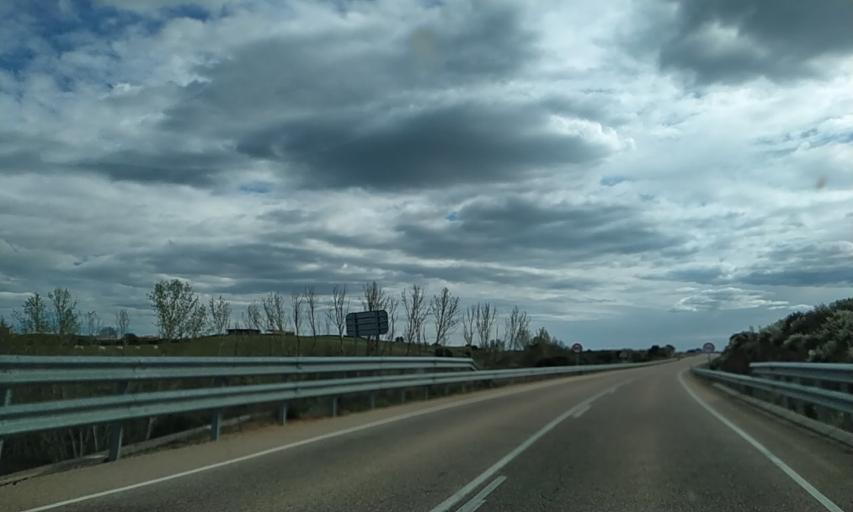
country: ES
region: Castille and Leon
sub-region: Provincia de Salamanca
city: Herguijuela de Ciudad Rodrigo
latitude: 40.4922
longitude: -6.5802
